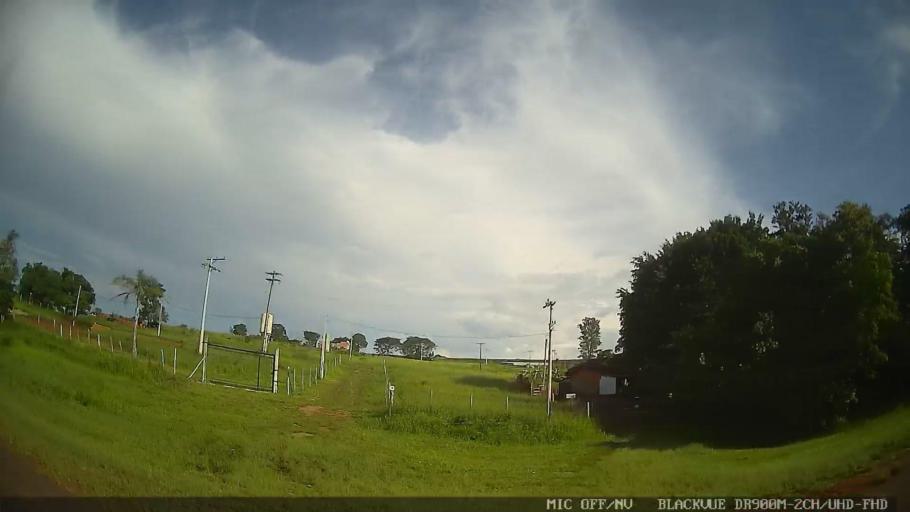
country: BR
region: Sao Paulo
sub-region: Tiete
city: Tiete
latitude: -23.0884
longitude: -47.6819
